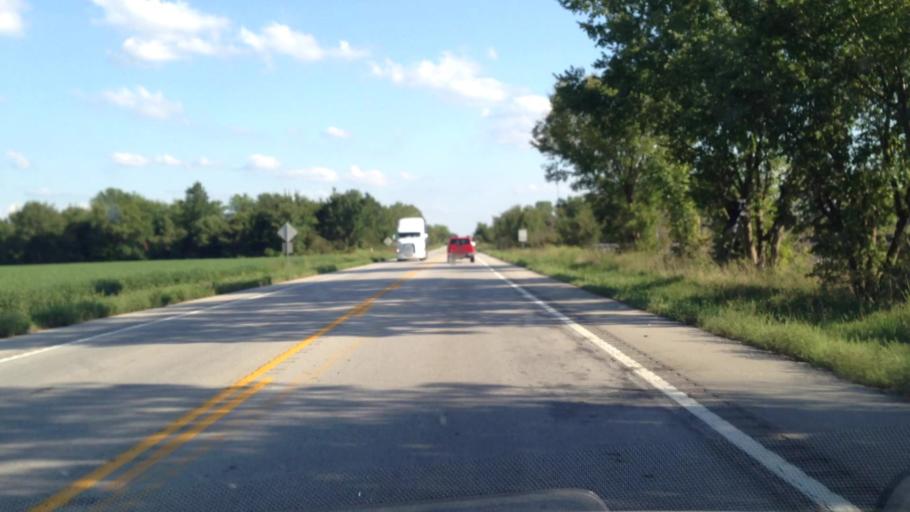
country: US
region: Missouri
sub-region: Jasper County
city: Carl Junction
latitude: 37.2718
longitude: -94.6006
